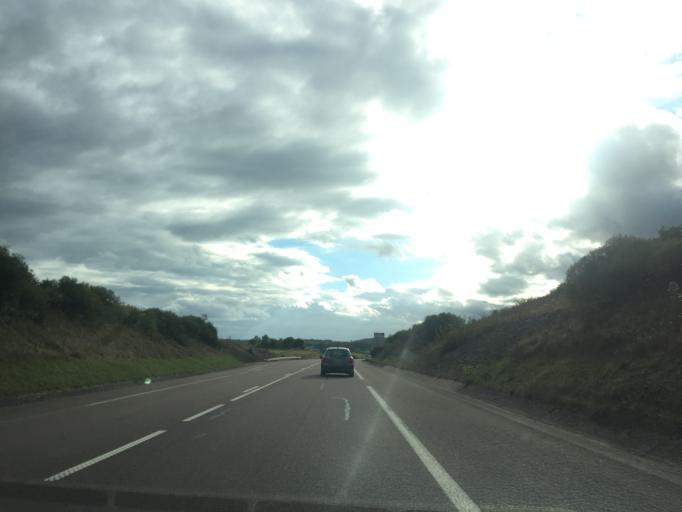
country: FR
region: Lorraine
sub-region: Departement des Vosges
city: Chatenois
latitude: 48.2957
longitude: 5.9055
